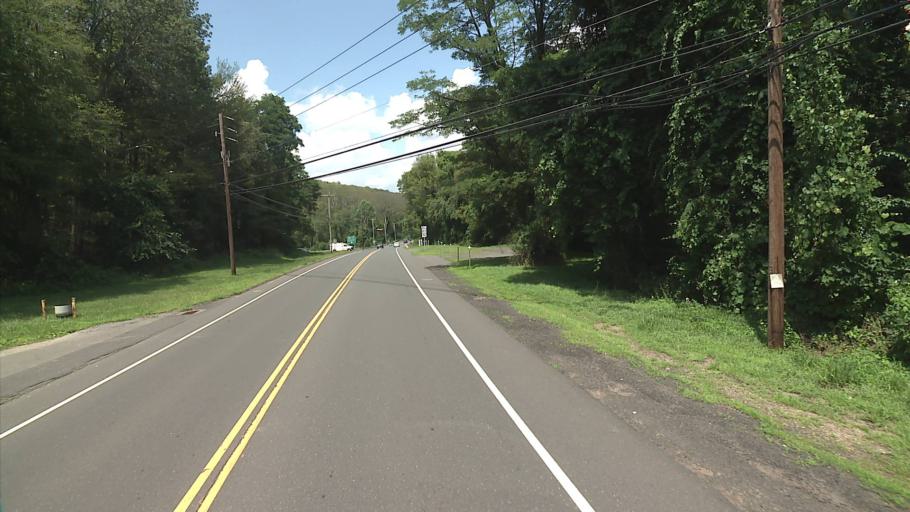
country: US
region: Connecticut
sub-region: Middlesex County
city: East Haddam
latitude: 41.4433
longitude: -72.4695
